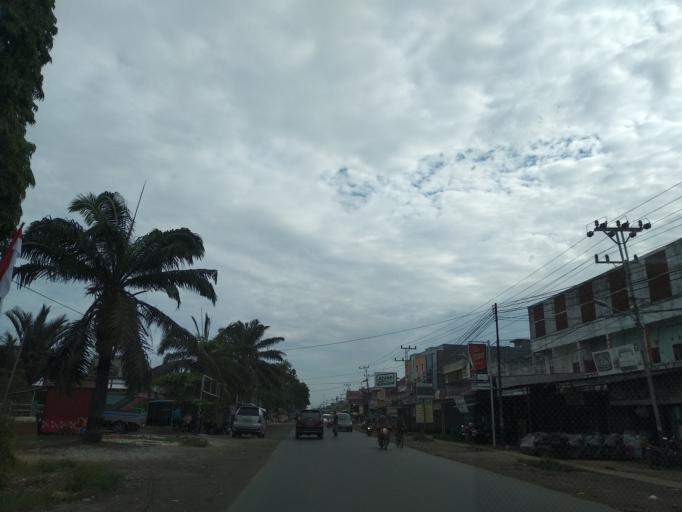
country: ID
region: South Kalimantan
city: Banjarmasin
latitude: -3.2736
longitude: 114.5993
